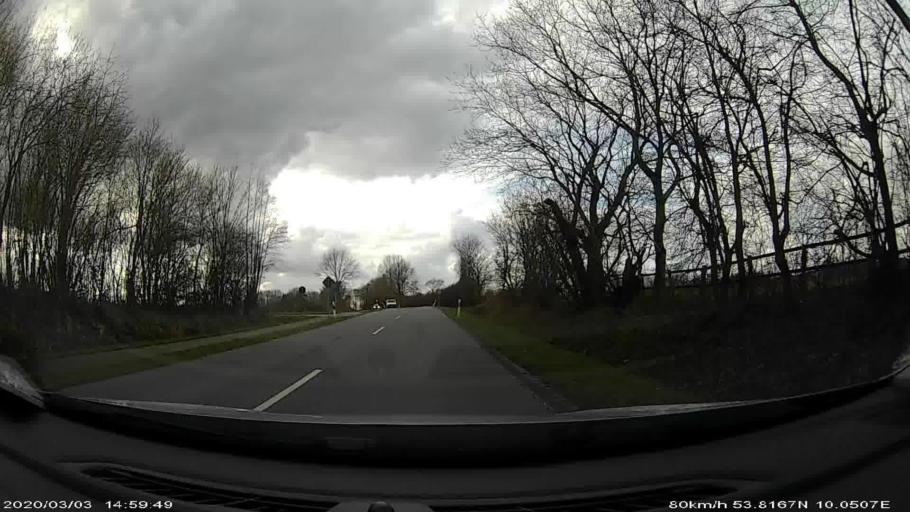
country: DE
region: Schleswig-Holstein
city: Huttblek
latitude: 53.8168
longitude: 10.0515
